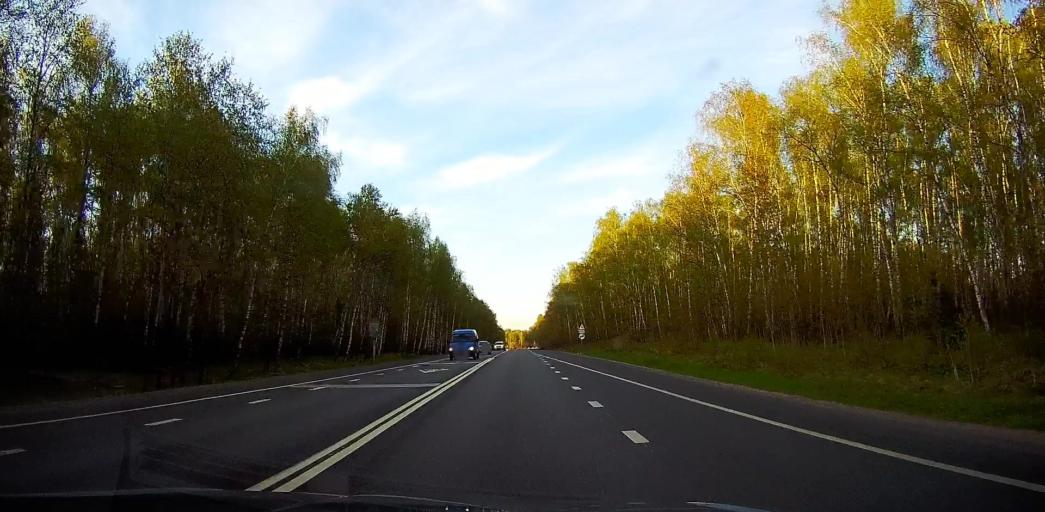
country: RU
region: Moskovskaya
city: Meshcherino
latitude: 55.2243
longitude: 38.4031
